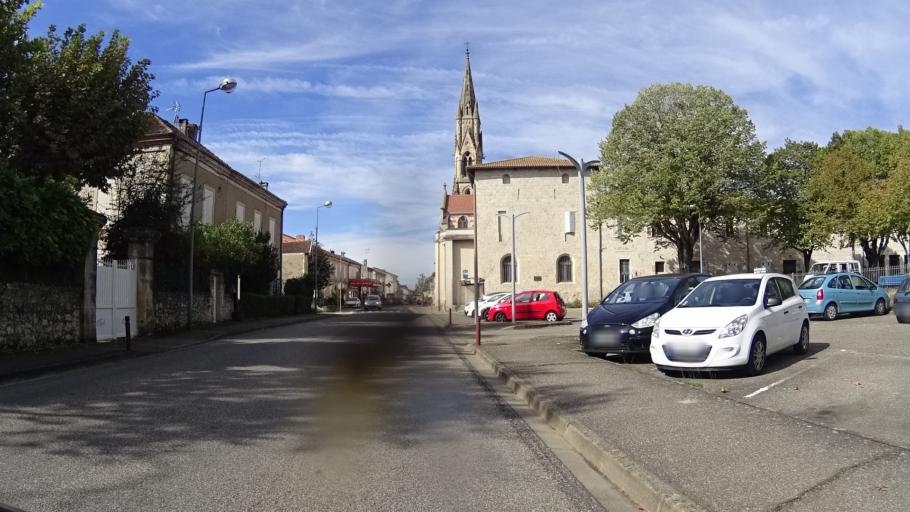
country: FR
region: Aquitaine
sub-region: Departement du Lot-et-Garonne
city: Bon-Encontre
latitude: 44.1862
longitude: 0.6727
